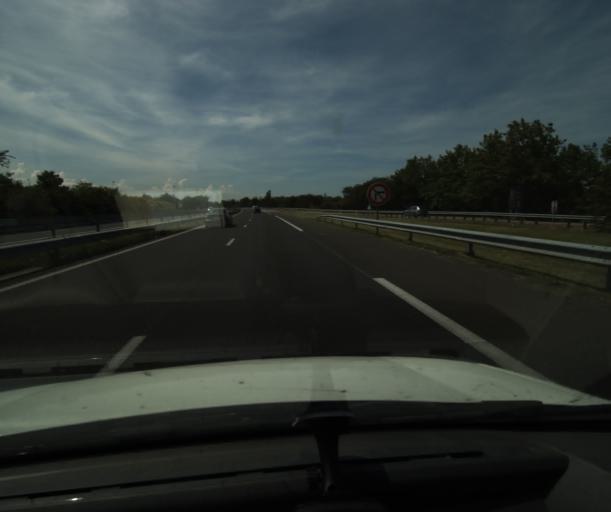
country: FR
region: Midi-Pyrenees
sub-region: Departement de la Haute-Garonne
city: Avignonet-Lauragais
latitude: 43.3532
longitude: 1.8077
